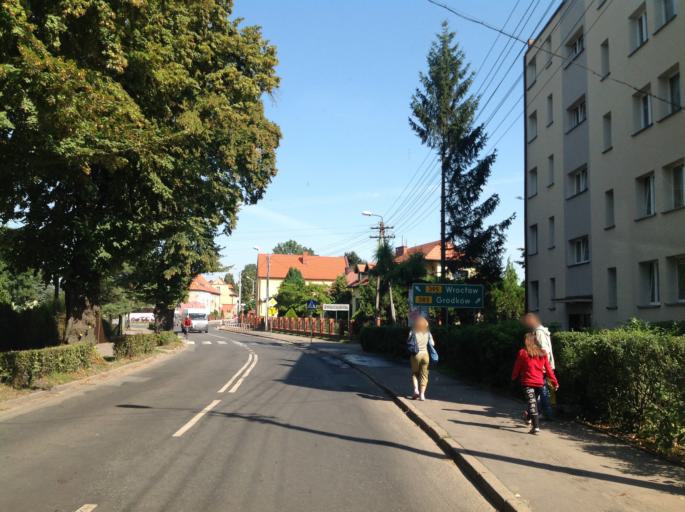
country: PL
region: Lower Silesian Voivodeship
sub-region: Powiat zabkowicki
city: Ziebice
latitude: 50.6049
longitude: 17.0489
